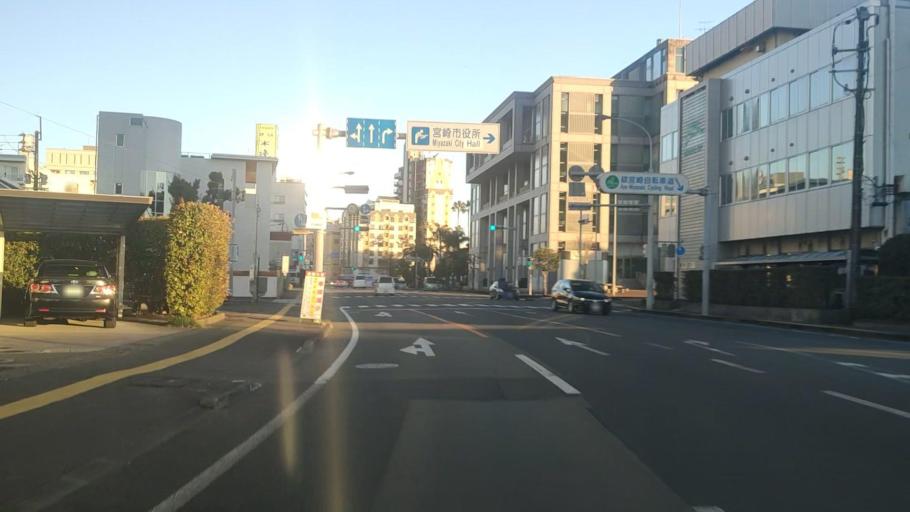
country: JP
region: Miyazaki
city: Miyazaki-shi
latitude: 31.9090
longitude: 131.4196
